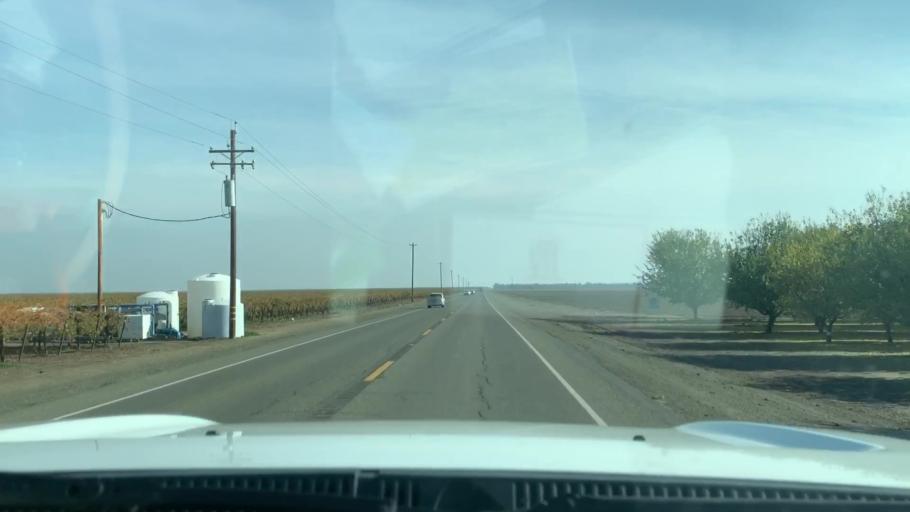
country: US
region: California
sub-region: Fresno County
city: Huron
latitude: 36.2549
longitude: -120.2026
